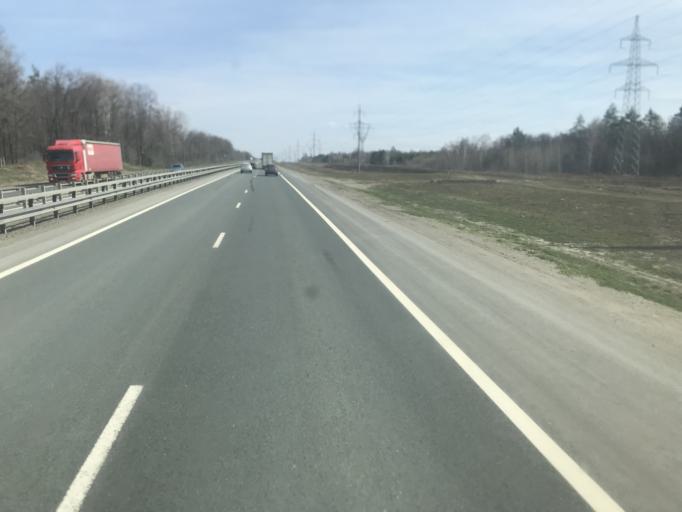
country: RU
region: Samara
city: Povolzhskiy
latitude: 53.5176
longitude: 49.7850
